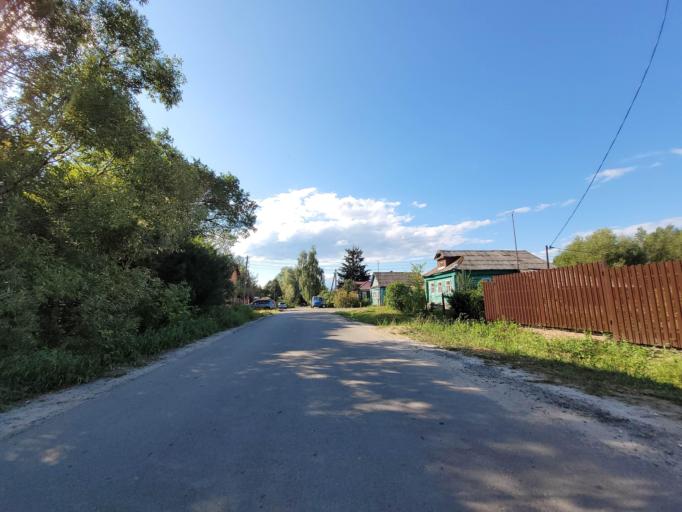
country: RU
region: Moskovskaya
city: Konobeyevo
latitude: 55.4109
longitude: 38.6975
